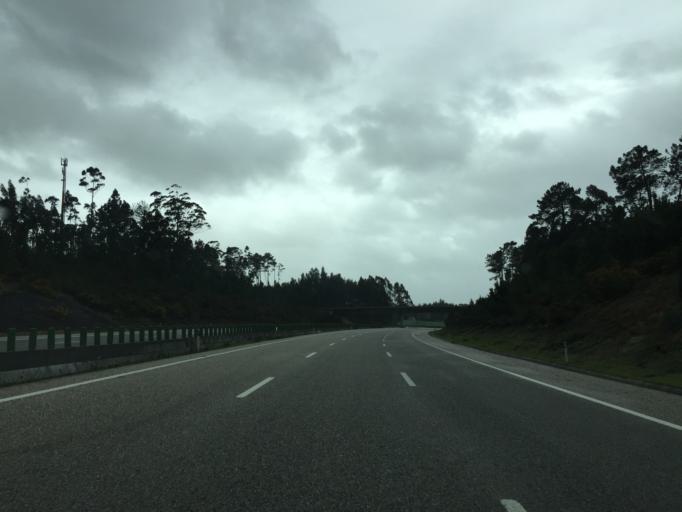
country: PT
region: Leiria
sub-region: Leiria
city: Monte Redondo
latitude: 39.9288
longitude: -8.7806
